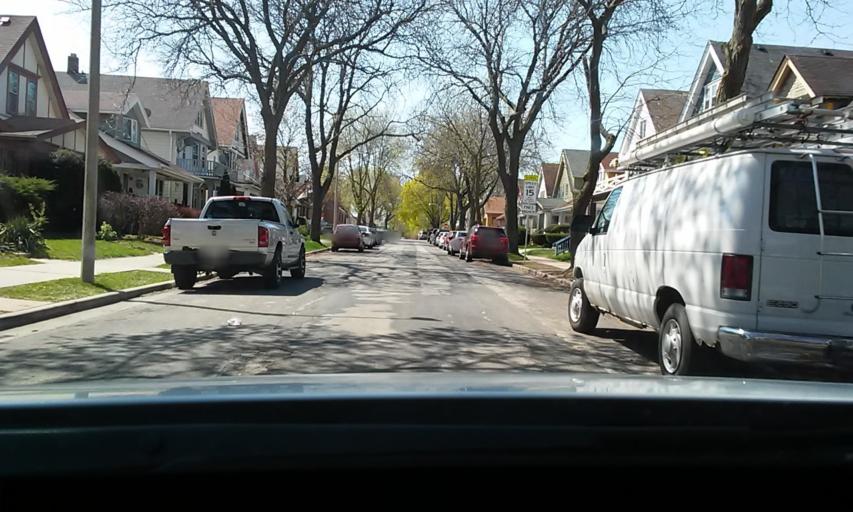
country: US
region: Wisconsin
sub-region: Milwaukee County
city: West Milwaukee
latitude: 43.0078
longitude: -87.9517
